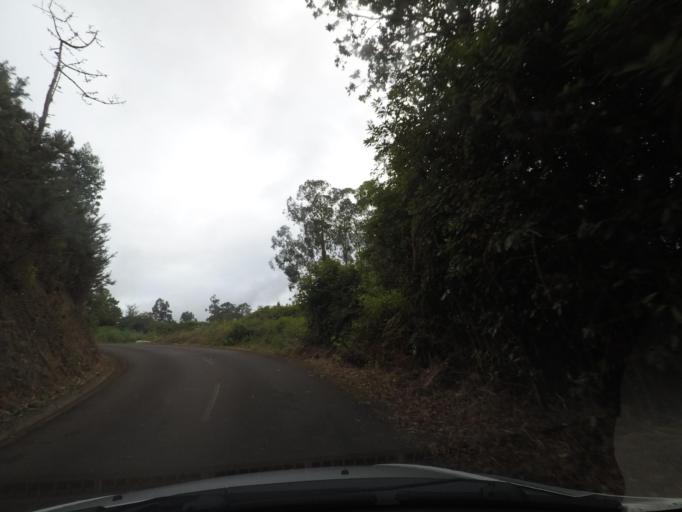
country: PT
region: Madeira
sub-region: Santana
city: Santana
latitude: 32.7840
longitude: -16.8778
